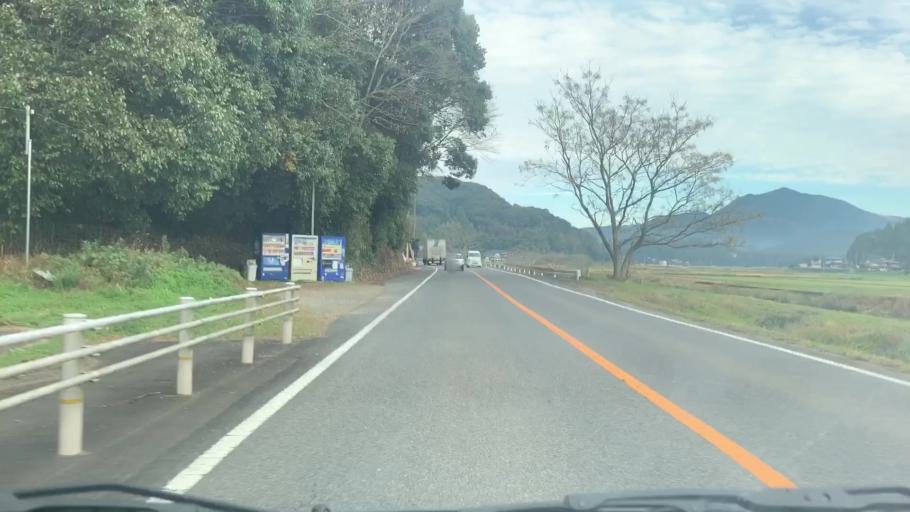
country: JP
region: Saga Prefecture
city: Takeocho-takeo
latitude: 33.2341
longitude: 129.9669
